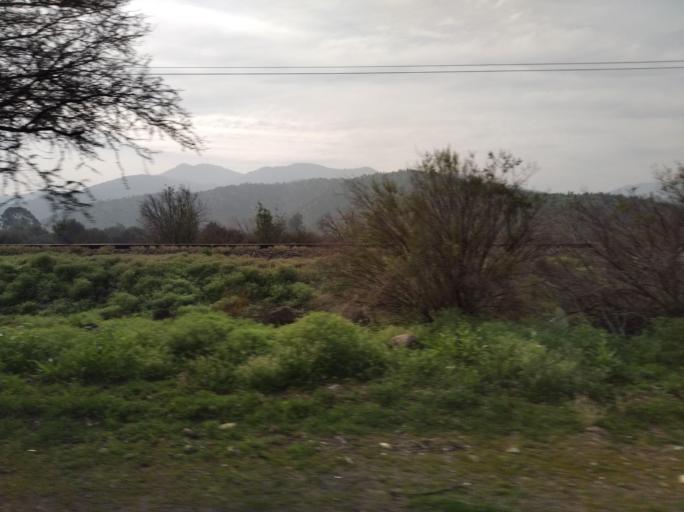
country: CL
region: Santiago Metropolitan
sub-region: Provincia de Chacabuco
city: Lampa
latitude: -33.1179
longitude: -70.9259
